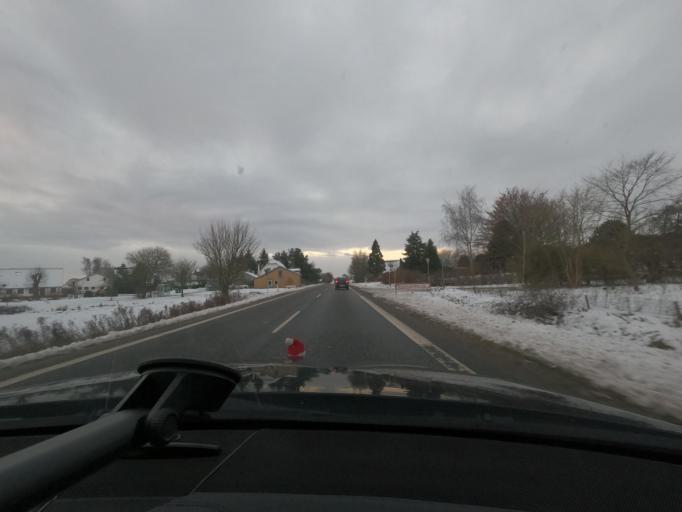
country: DE
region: Schleswig-Holstein
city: Wees
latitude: 54.8811
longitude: 9.4768
